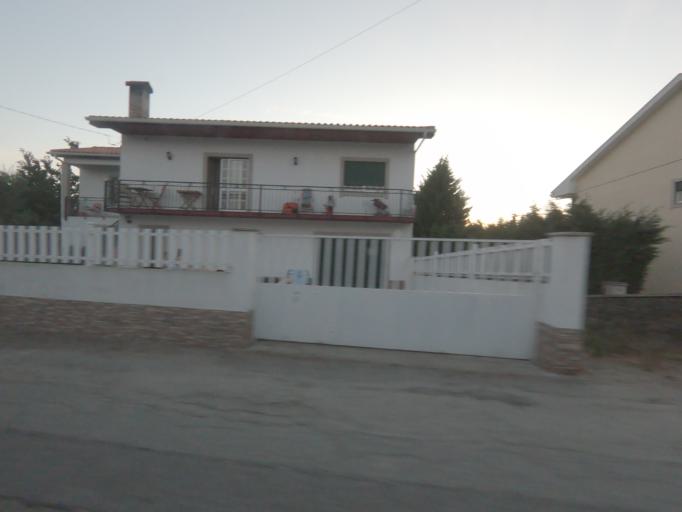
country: PT
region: Vila Real
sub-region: Peso da Regua
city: Peso da Regua
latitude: 41.1839
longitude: -7.7190
